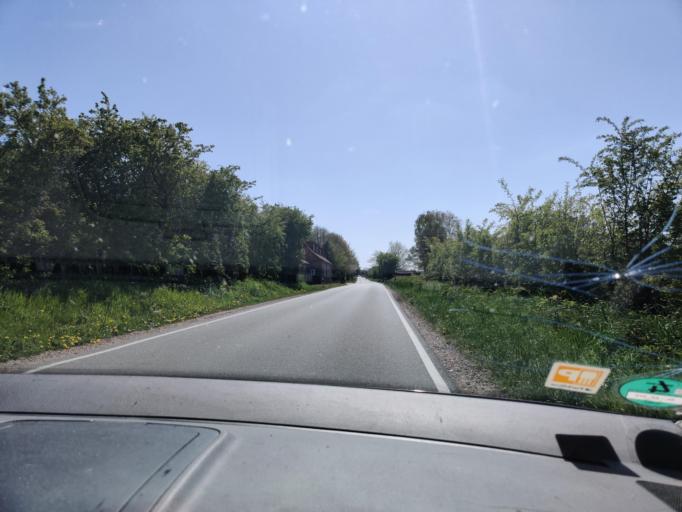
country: DE
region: Schleswig-Holstein
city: Tarp
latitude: 54.6934
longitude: 9.3887
